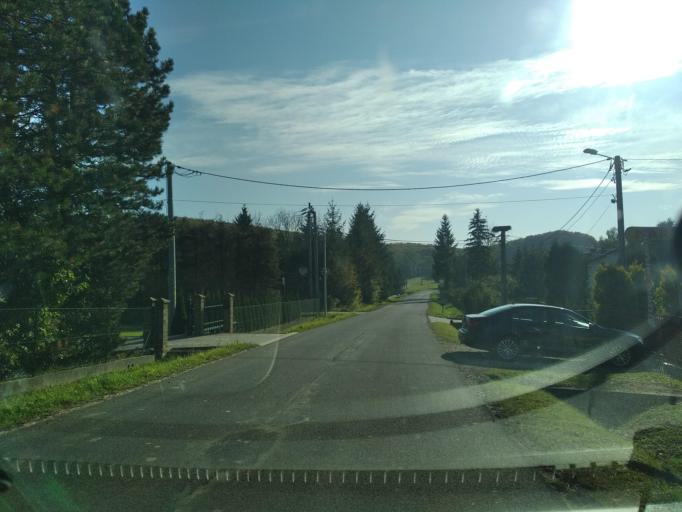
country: PL
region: Subcarpathian Voivodeship
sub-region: Powiat sanocki
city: Besko
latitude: 49.5752
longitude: 21.9469
